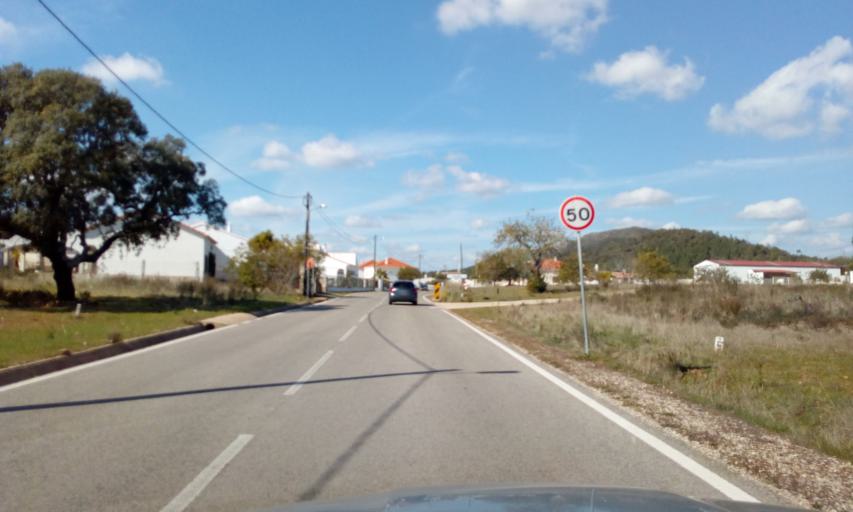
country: PT
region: Faro
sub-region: Loule
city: Loule
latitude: 37.2444
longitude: -8.0628
